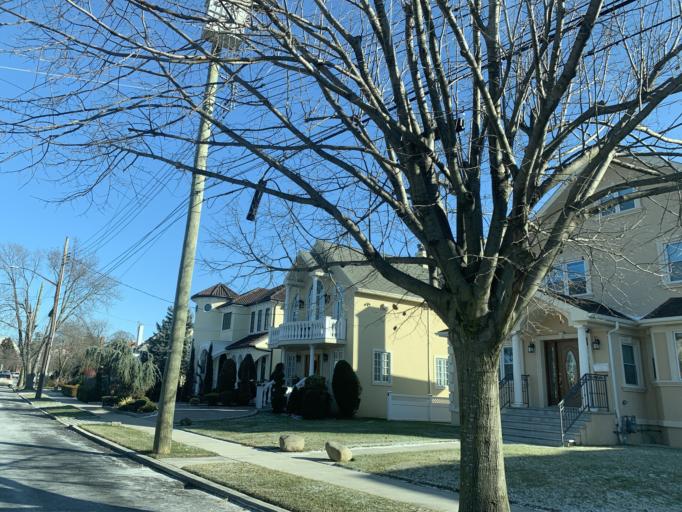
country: US
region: New York
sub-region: Bronx
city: The Bronx
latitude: 40.7909
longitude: -73.8282
